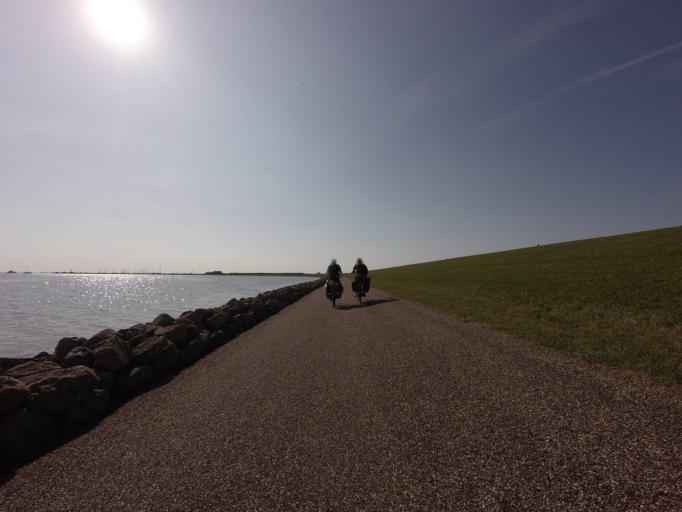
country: NL
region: Friesland
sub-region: Gemeente Schiermonnikoog
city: Schiermonnikoog
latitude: 53.4724
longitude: 6.1757
